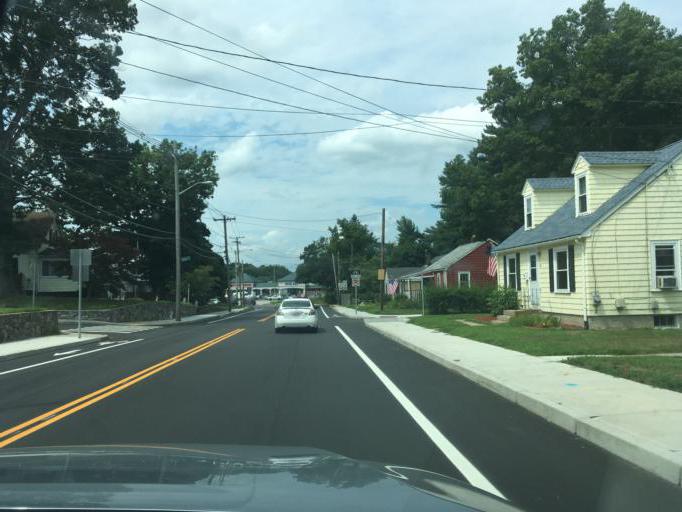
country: US
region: Rhode Island
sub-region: Kent County
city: West Warwick
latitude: 41.6817
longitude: -71.5585
